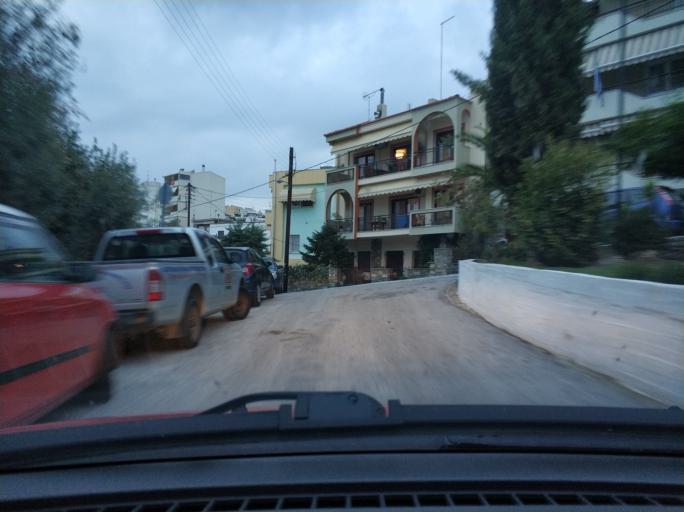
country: GR
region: East Macedonia and Thrace
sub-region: Nomos Kavalas
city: Kavala
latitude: 40.9248
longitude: 24.3883
